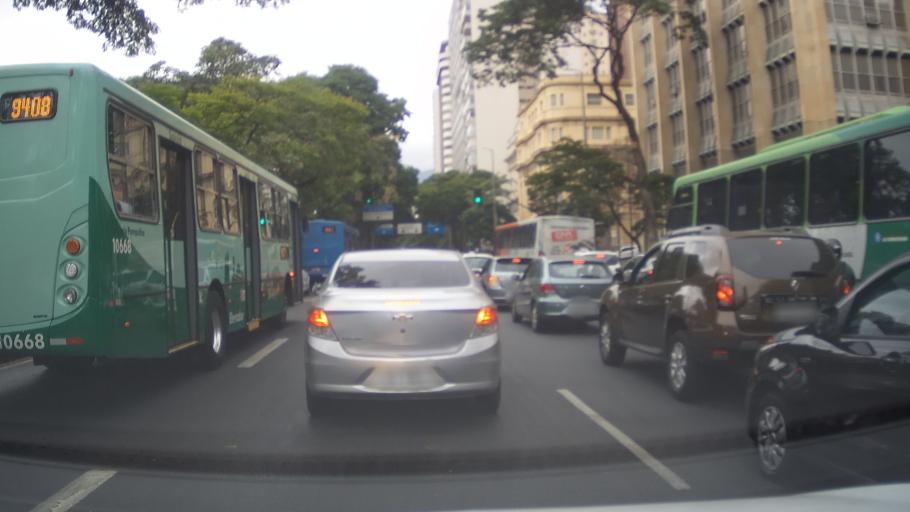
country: BR
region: Minas Gerais
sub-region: Belo Horizonte
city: Belo Horizonte
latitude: -19.9239
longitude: -43.9358
